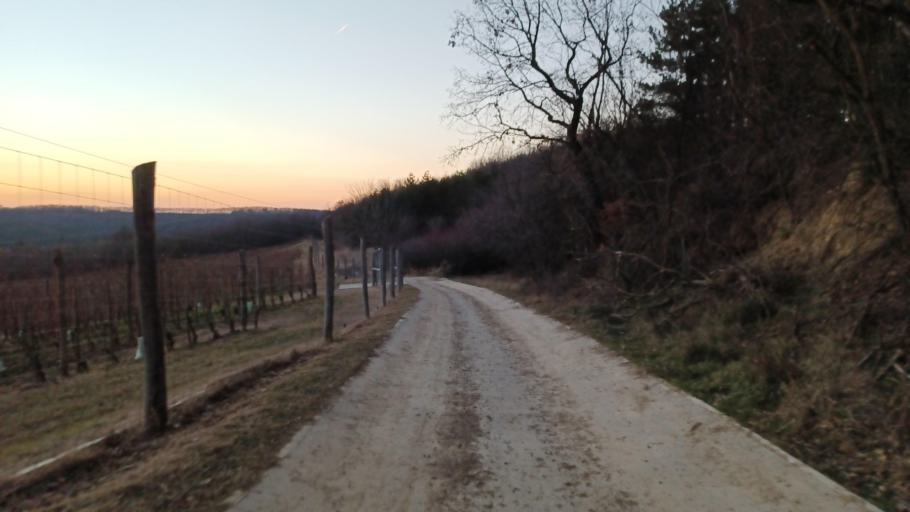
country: HU
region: Tolna
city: Szentgalpuszta
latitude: 46.3460
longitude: 18.6333
